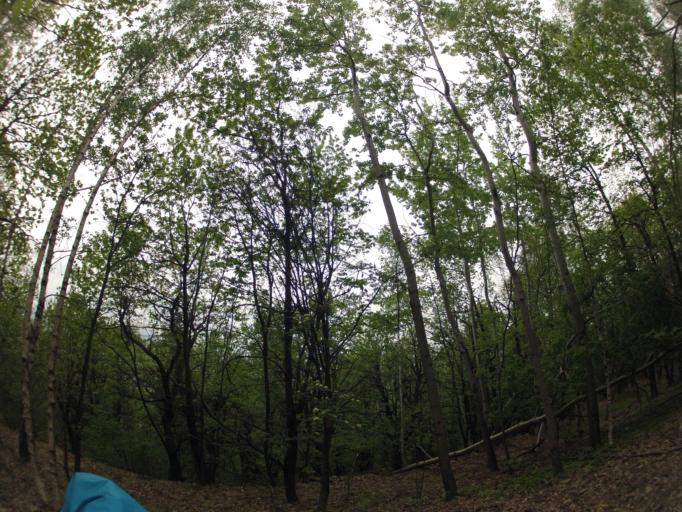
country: IT
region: Piedmont
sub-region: Provincia di Cuneo
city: Peveragno
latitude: 44.3259
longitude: 7.5928
